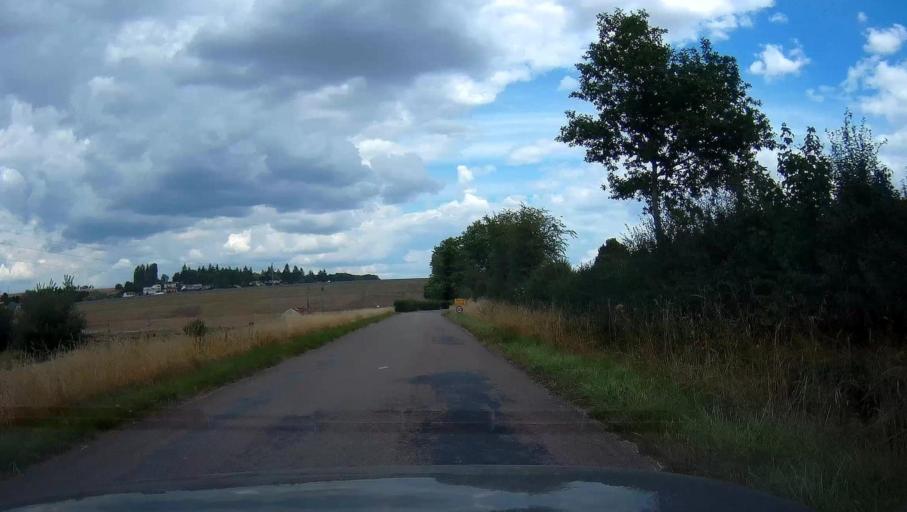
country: FR
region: Champagne-Ardenne
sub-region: Departement de la Haute-Marne
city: Langres
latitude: 47.8639
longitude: 5.3715
